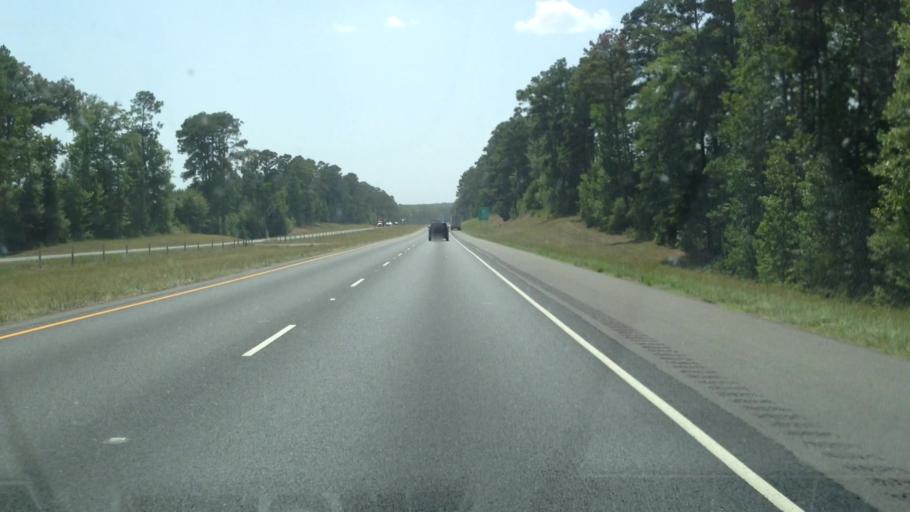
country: US
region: Louisiana
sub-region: Webster Parish
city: Minden
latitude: 32.5622
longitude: -93.1347
